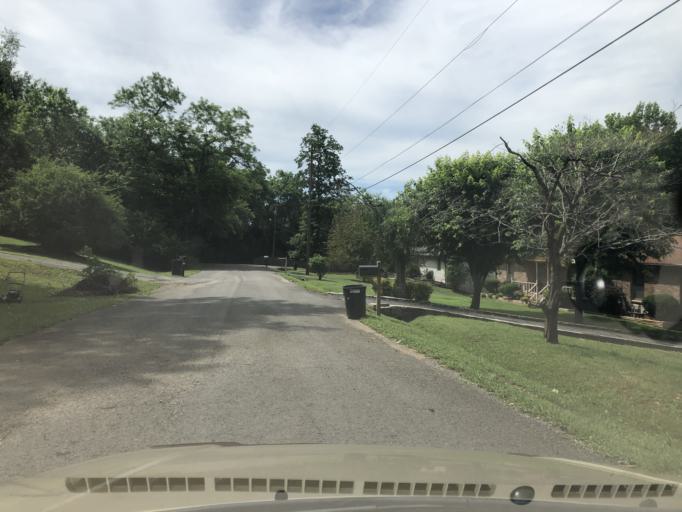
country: US
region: Tennessee
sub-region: Davidson County
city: Lakewood
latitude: 36.2575
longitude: -86.6220
